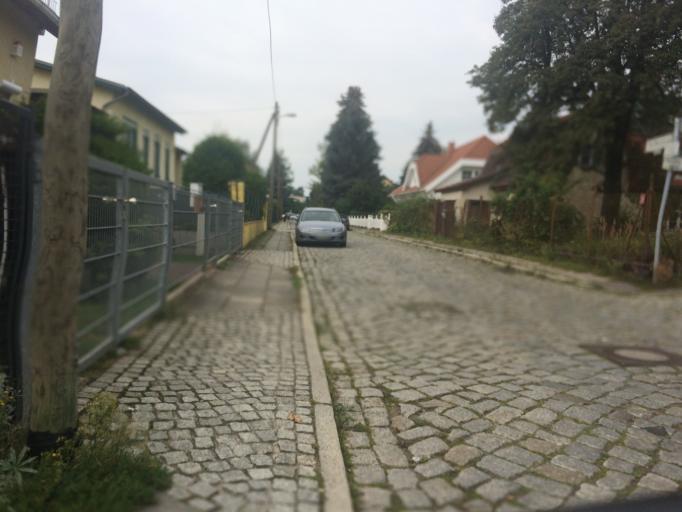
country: DE
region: Berlin
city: Heinersdorf
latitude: 52.5665
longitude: 13.4329
